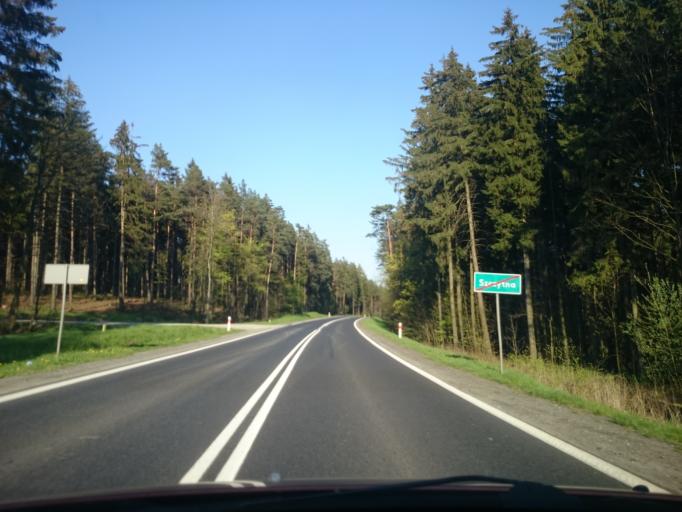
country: PL
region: Lower Silesian Voivodeship
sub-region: Powiat klodzki
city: Szczytna
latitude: 50.4258
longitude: 16.4754
